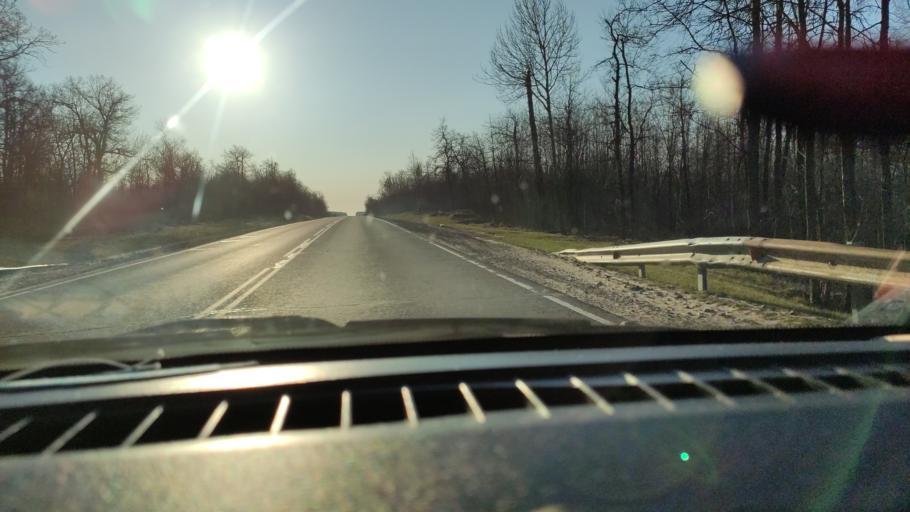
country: RU
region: Saratov
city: Vol'sk
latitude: 52.1101
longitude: 47.3613
